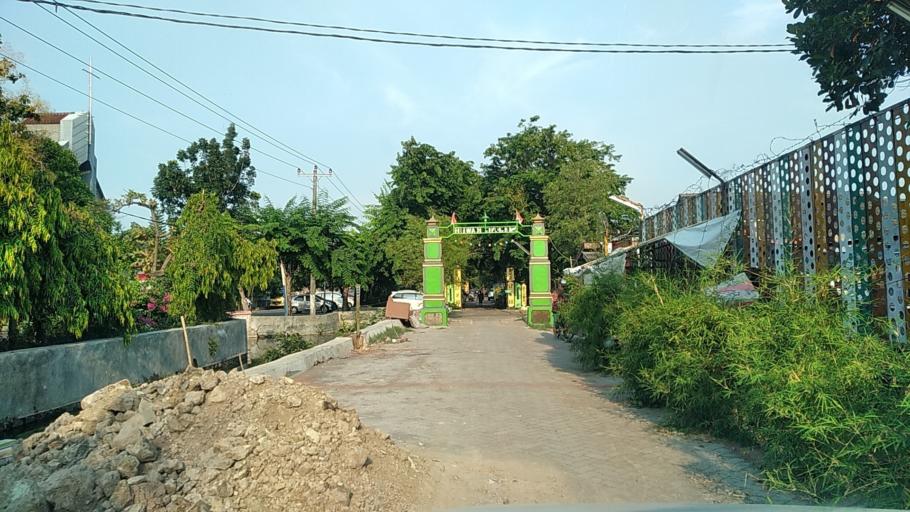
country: ID
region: Central Java
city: Semarang
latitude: -6.9650
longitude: 110.4067
